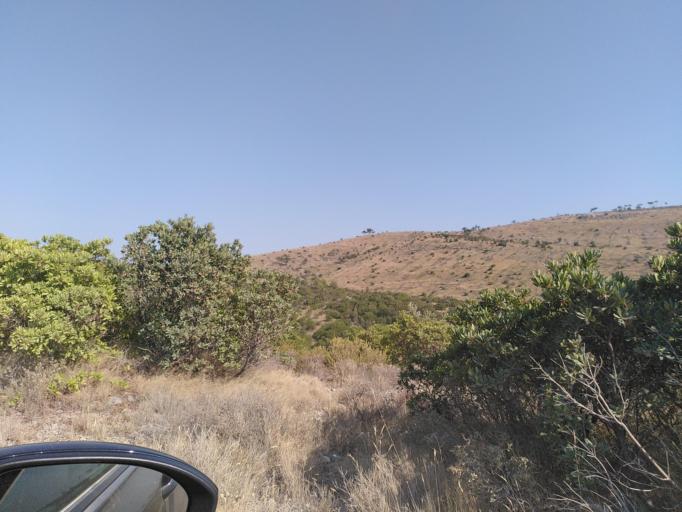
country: HR
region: Splitsko-Dalmatinska
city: Stari Grad
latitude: 43.1531
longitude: 16.5807
